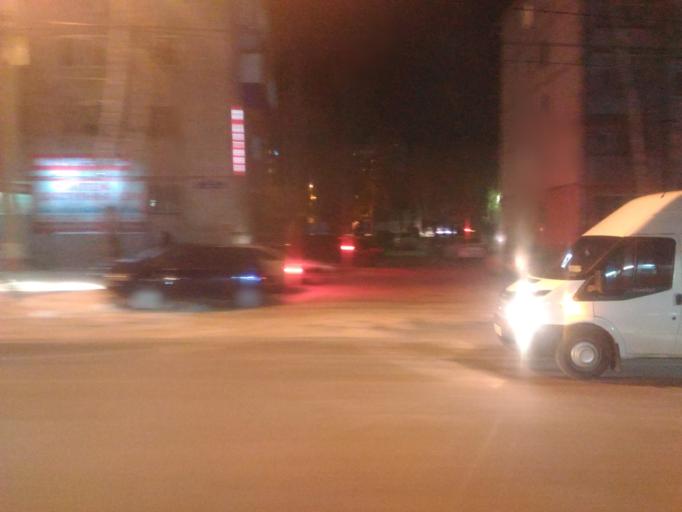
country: RU
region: Ulyanovsk
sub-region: Ulyanovskiy Rayon
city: Ulyanovsk
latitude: 54.3453
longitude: 48.3921
